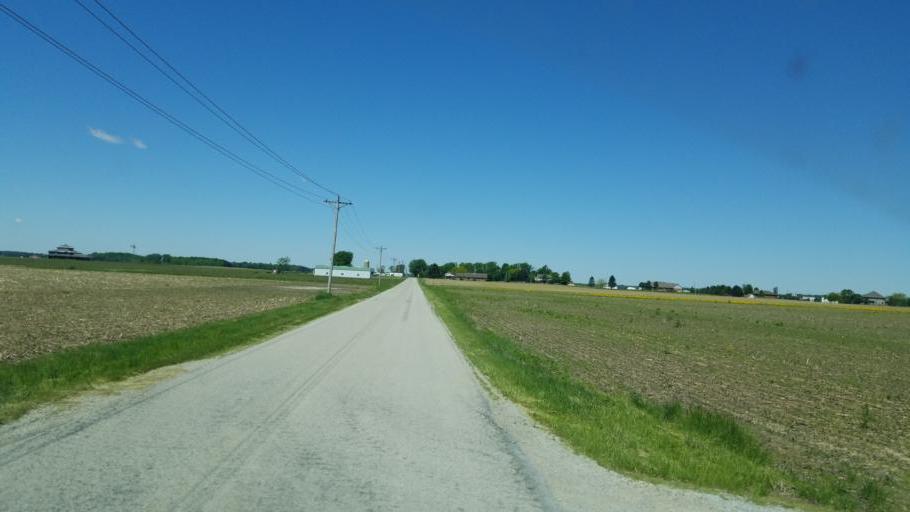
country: US
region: Ohio
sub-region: Shelby County
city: Anna
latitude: 40.3727
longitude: -84.2526
